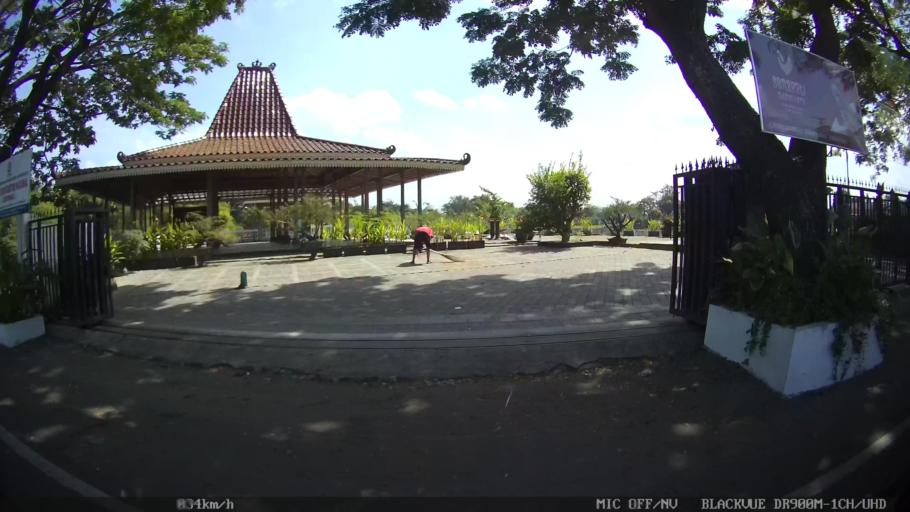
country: ID
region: Daerah Istimewa Yogyakarta
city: Sewon
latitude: -7.8363
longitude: 110.3756
